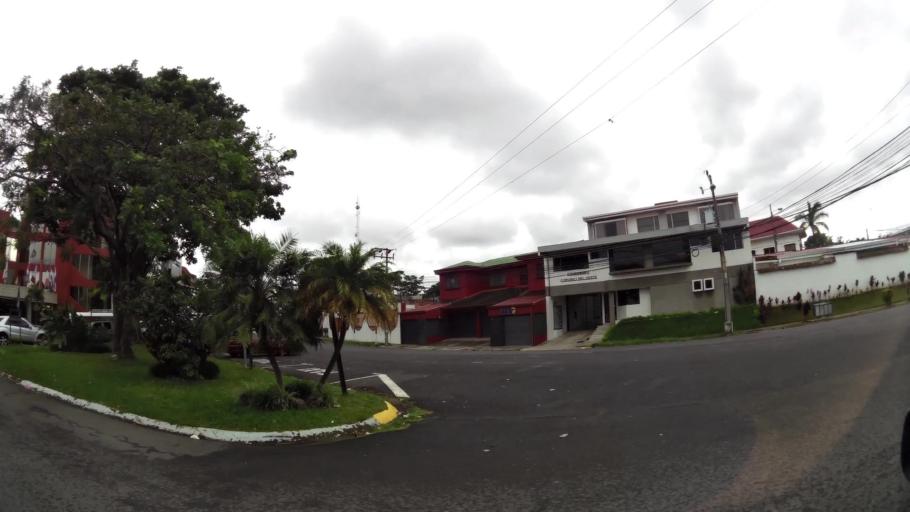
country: CR
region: San Jose
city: Colima
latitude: 9.9404
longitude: -84.1019
